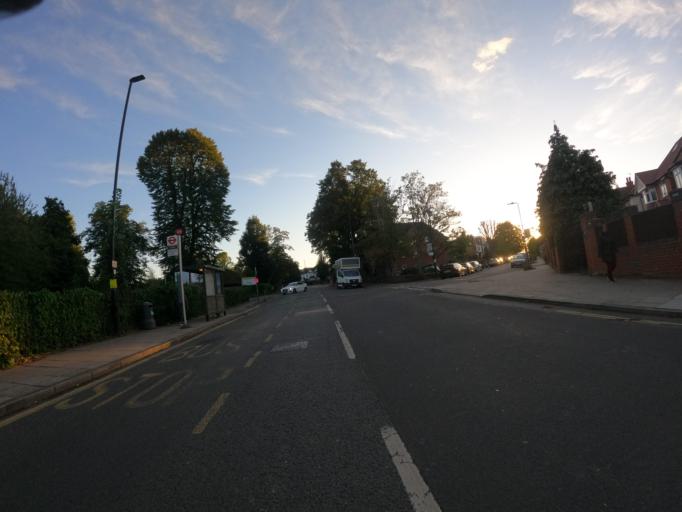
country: GB
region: England
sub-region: Greater London
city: Acton
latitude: 51.5112
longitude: -0.2569
